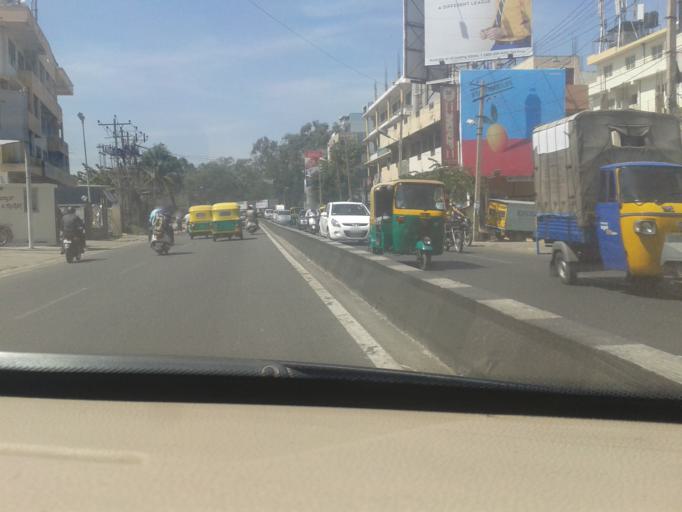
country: IN
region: Karnataka
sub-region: Bangalore Urban
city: Bangalore
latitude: 12.9502
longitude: 77.5927
